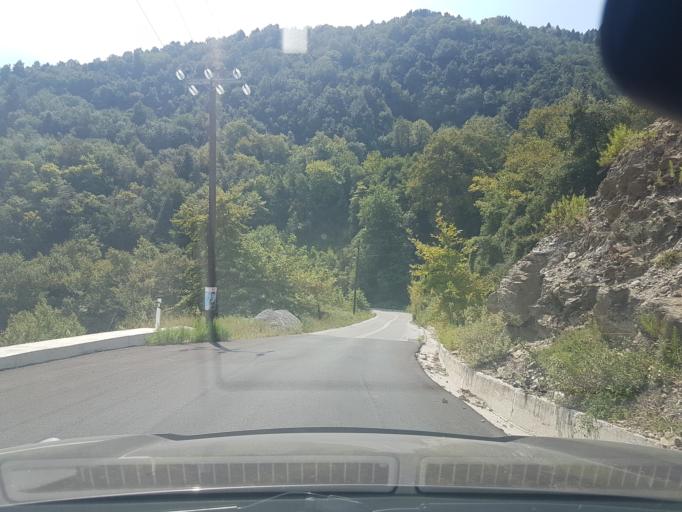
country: GR
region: Central Greece
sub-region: Nomos Evvoias
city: Kymi
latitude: 38.6398
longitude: 23.9402
